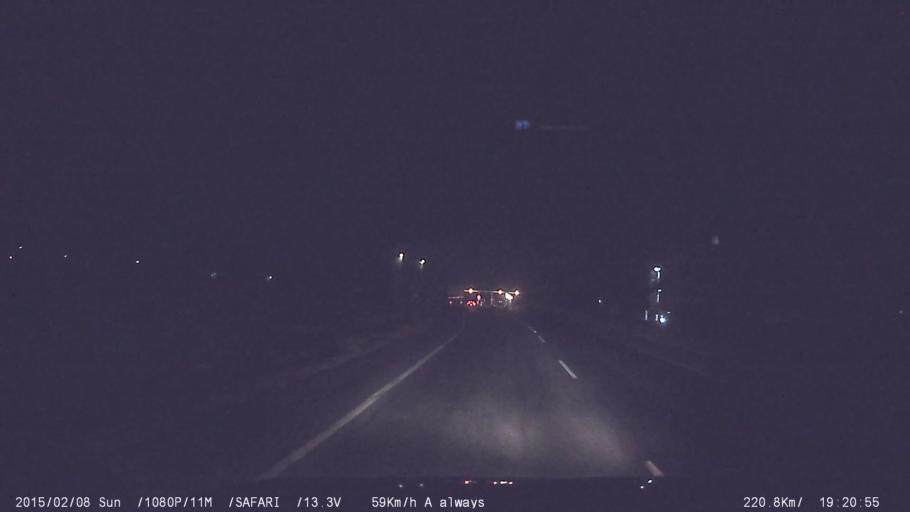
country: IN
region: Tamil Nadu
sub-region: Coimbatore
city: Madukkarai
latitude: 10.9124
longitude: 76.9807
